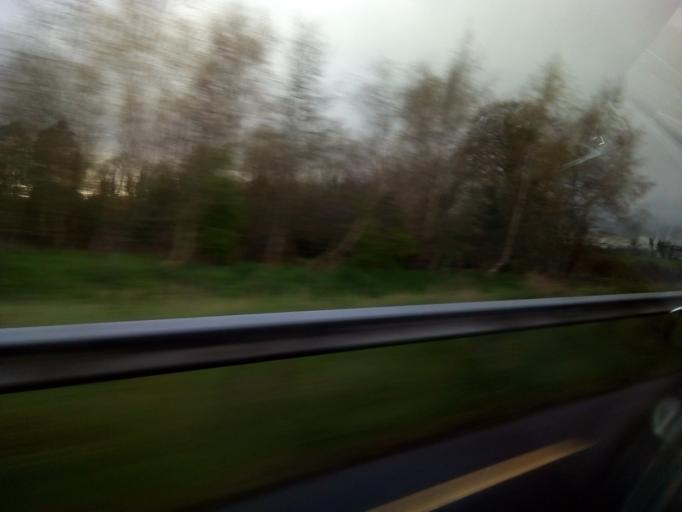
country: IE
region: Leinster
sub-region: An Longfort
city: Longford
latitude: 53.8264
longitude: -7.9102
